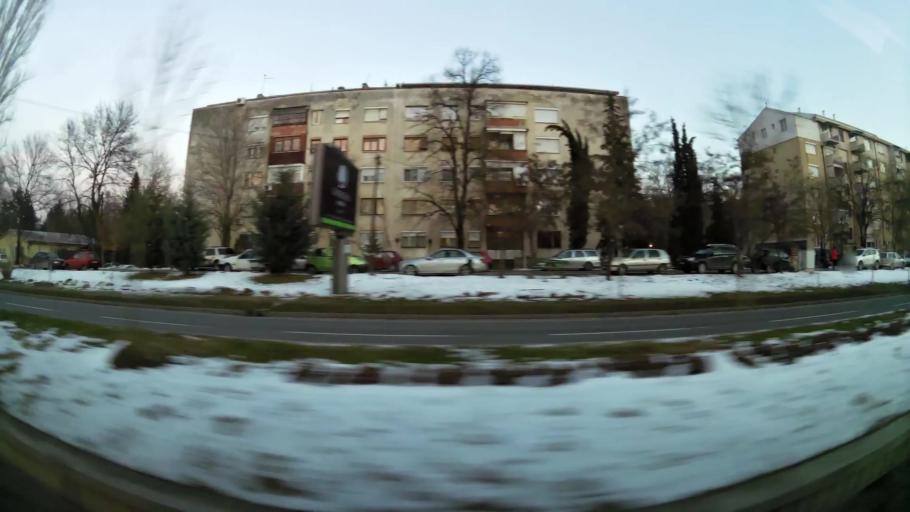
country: MK
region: Karpos
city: Skopje
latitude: 42.0040
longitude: 21.4051
